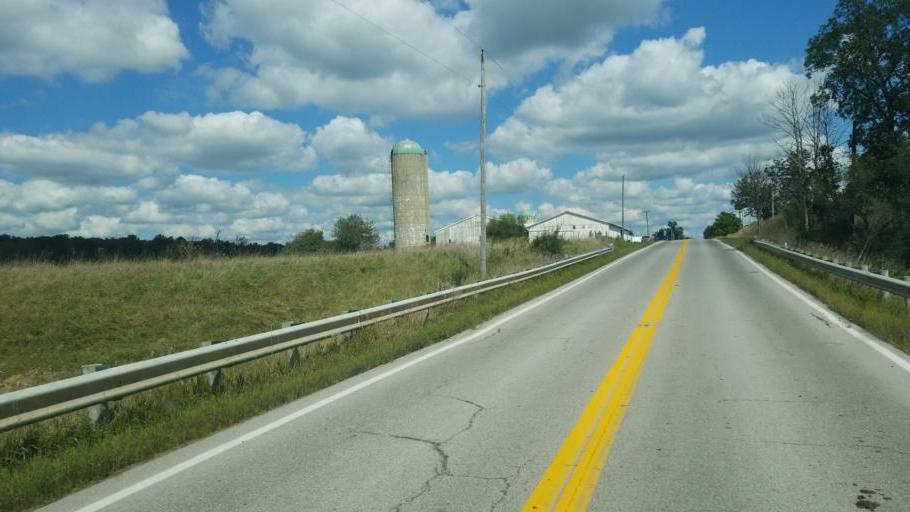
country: US
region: Ohio
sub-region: Wayne County
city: West Salem
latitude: 40.9765
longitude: -82.2393
